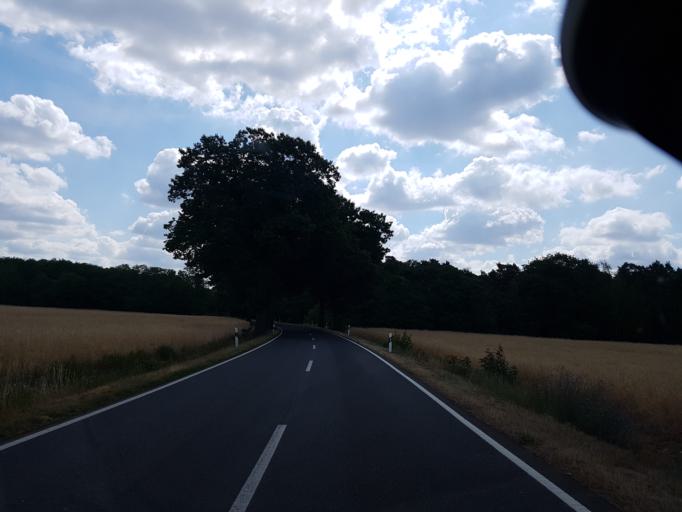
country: DE
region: Brandenburg
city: Altdobern
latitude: 51.6886
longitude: 14.1031
